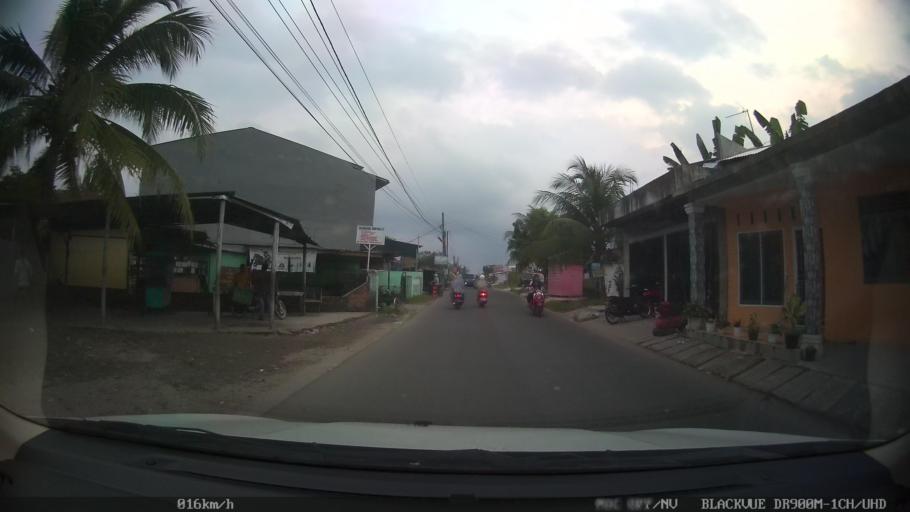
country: ID
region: North Sumatra
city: Sunggal
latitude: 3.5640
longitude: 98.5979
